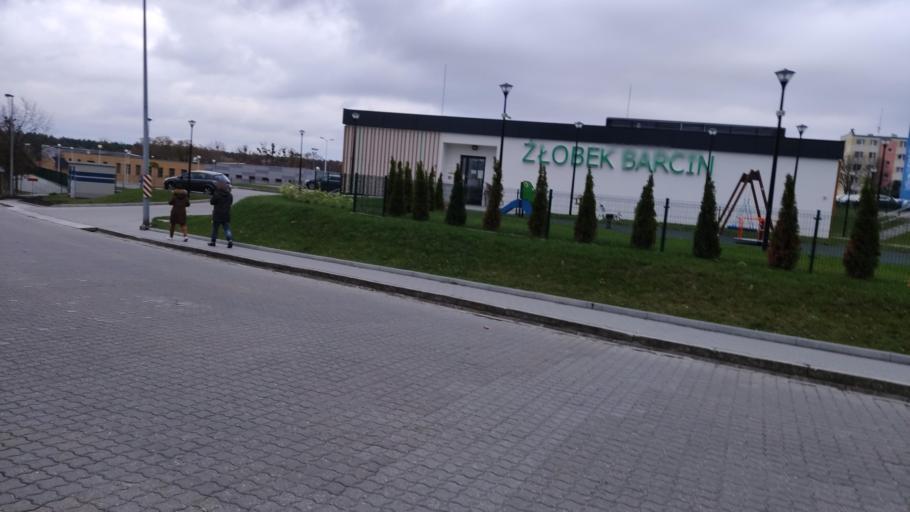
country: PL
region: Kujawsko-Pomorskie
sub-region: Powiat zninski
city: Barcin
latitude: 52.8545
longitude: 17.9447
